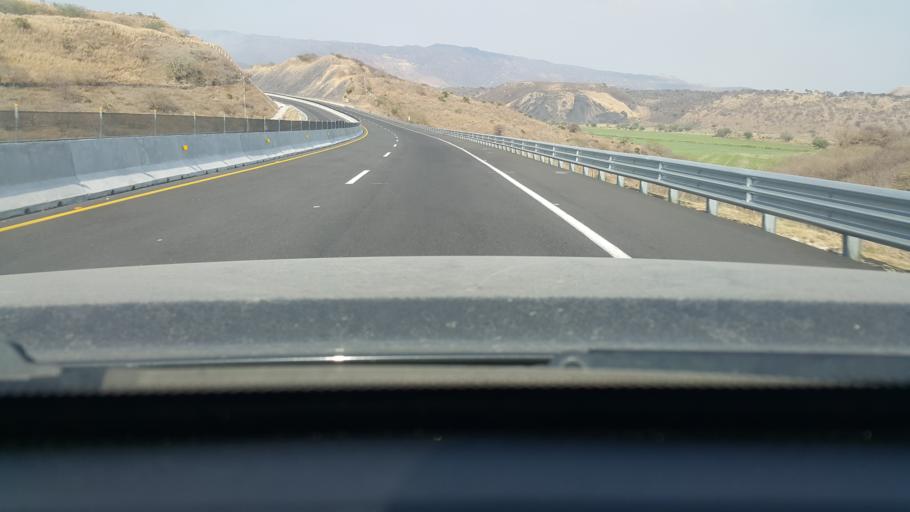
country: MX
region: Nayarit
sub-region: Ahuacatlan
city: Ahuacatlan
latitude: 21.0675
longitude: -104.4642
